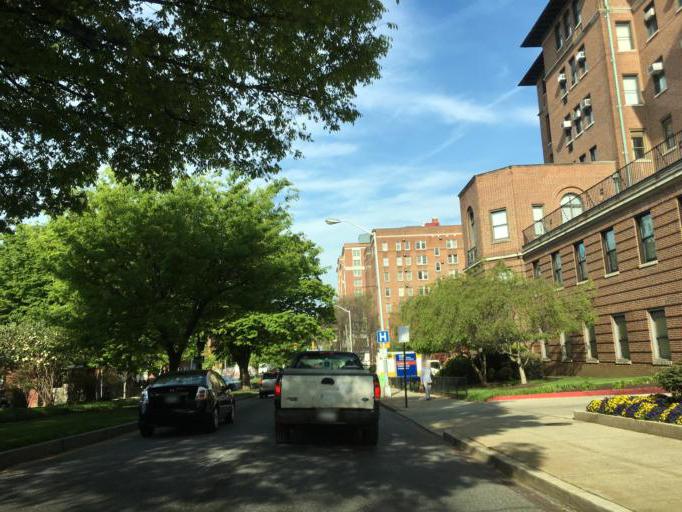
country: US
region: Maryland
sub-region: City of Baltimore
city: Baltimore
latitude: 39.3283
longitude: -76.6141
